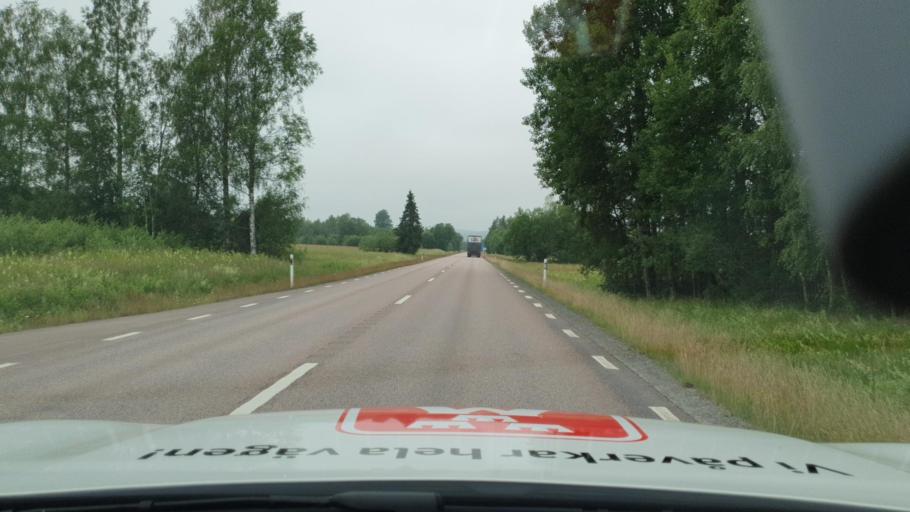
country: SE
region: Vaermland
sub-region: Sunne Kommun
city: Sunne
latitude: 59.7117
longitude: 13.1451
